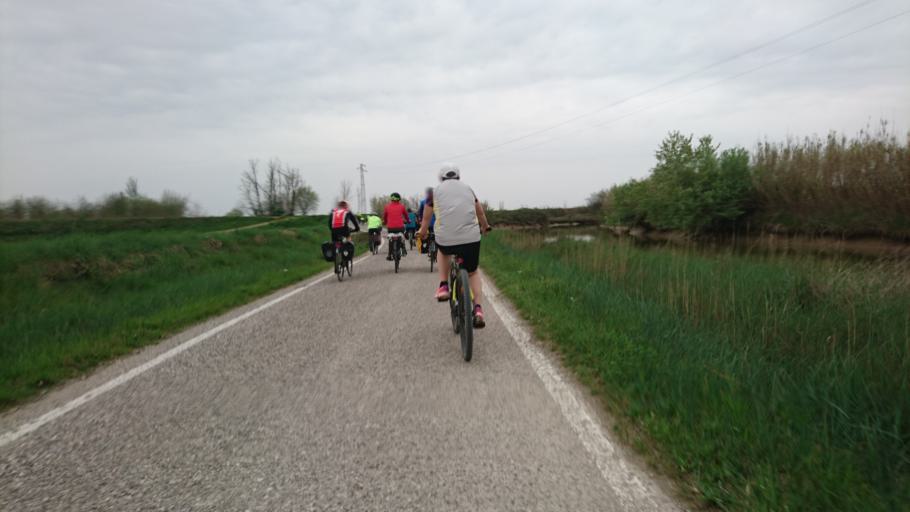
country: IT
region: Veneto
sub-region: Provincia di Venezia
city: Cesarolo
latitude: 45.6878
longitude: 12.9861
